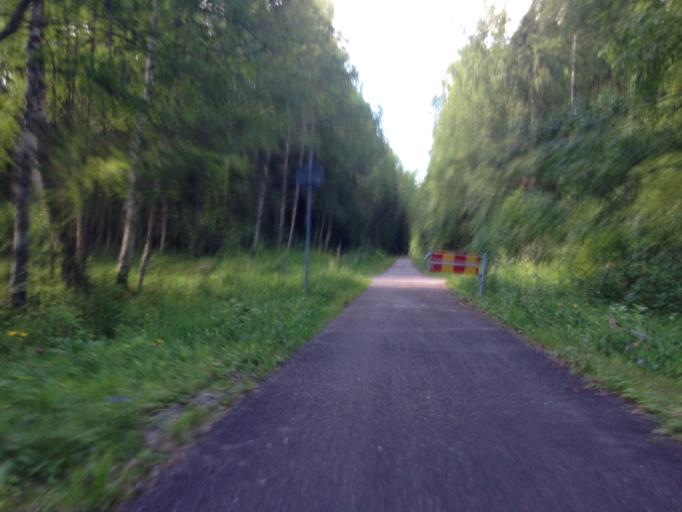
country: SE
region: Dalarna
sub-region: Ludvika Kommun
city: Grangesberg
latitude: 60.2077
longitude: 15.0547
